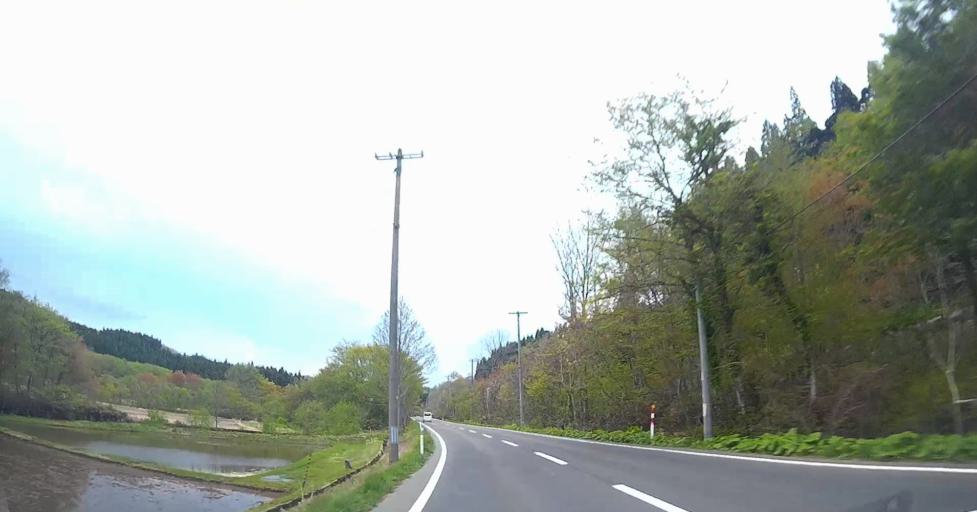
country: JP
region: Aomori
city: Goshogawara
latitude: 41.1241
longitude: 140.5202
